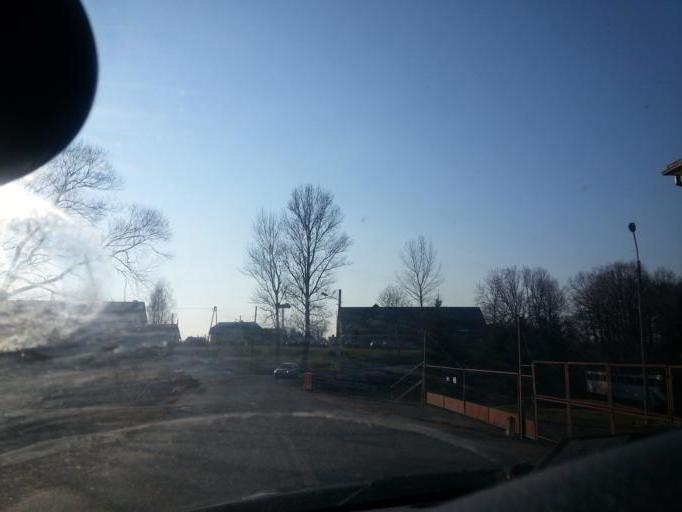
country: PL
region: Lower Silesian Voivodeship
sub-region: Powiat jeleniogorski
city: Myslakowice
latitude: 50.8278
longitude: 15.7958
